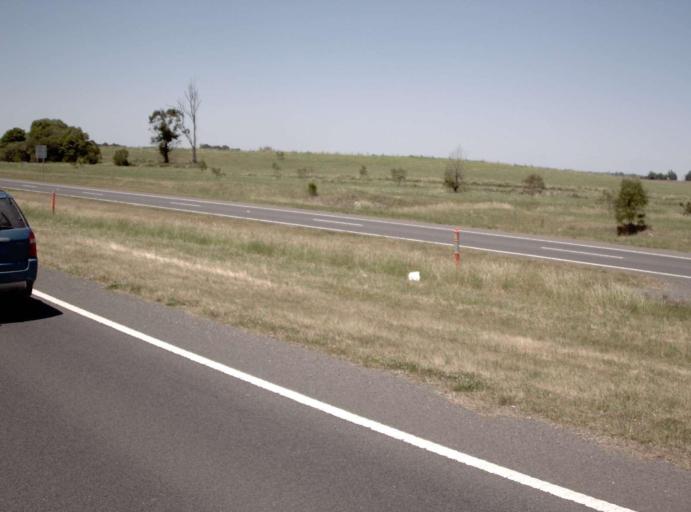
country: AU
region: Victoria
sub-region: Casey
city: Berwick
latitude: -38.0618
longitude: 145.3702
